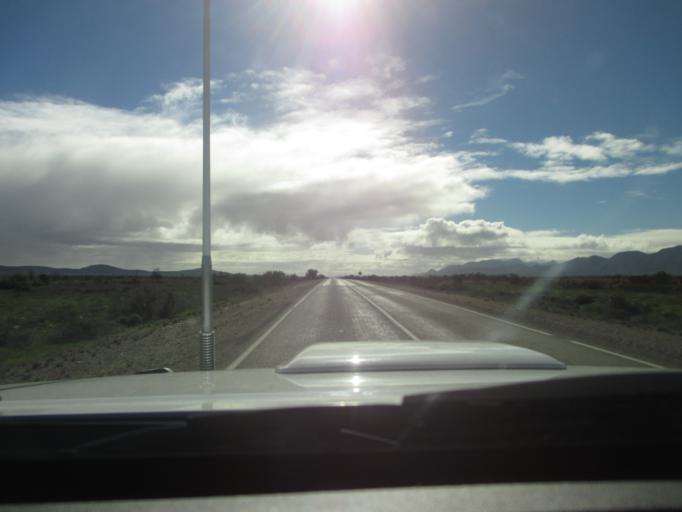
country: AU
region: South Australia
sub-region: Flinders Ranges
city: Quorn
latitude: -31.6979
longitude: 138.3581
